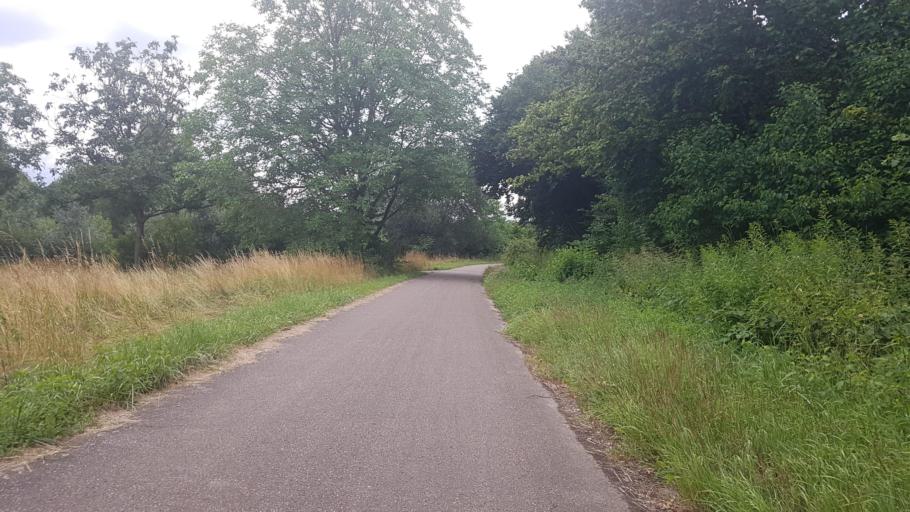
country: DE
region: Baden-Wuerttemberg
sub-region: Karlsruhe Region
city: Rheinau
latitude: 48.8832
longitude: 8.2064
